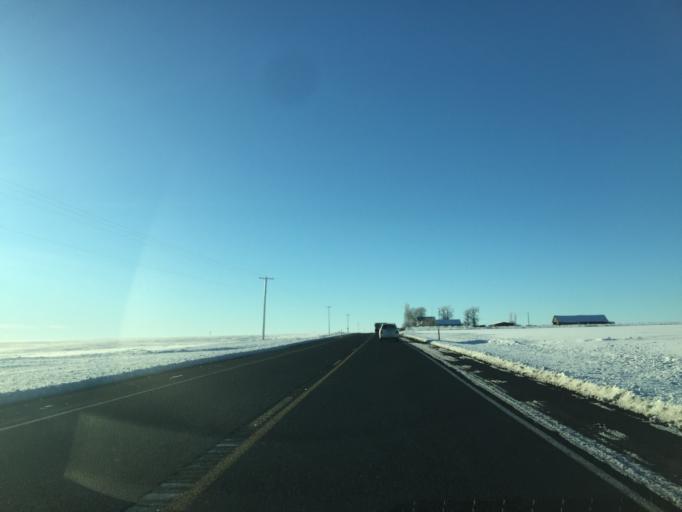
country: US
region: Washington
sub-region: Okanogan County
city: Coulee Dam
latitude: 47.6844
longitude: -119.0149
